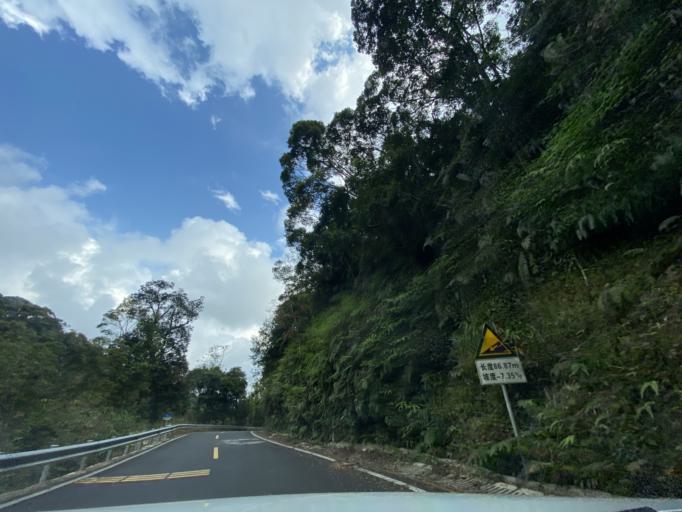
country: CN
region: Hainan
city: Diaoluoshan
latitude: 18.7219
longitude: 109.8738
